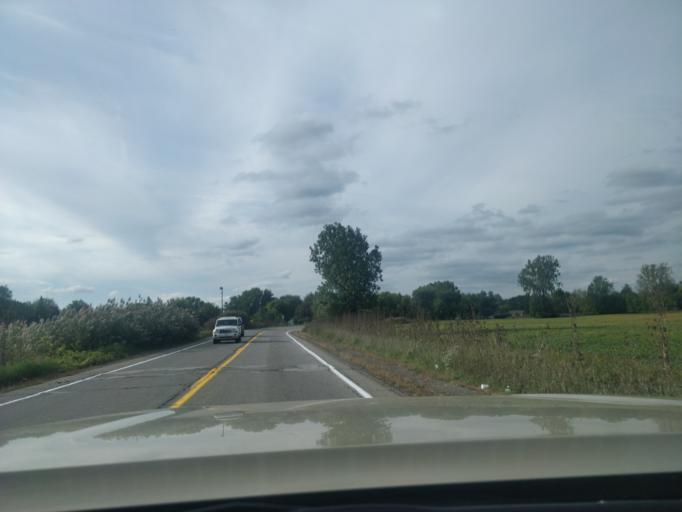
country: US
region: Michigan
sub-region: Wayne County
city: Romulus
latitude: 42.2241
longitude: -83.4427
